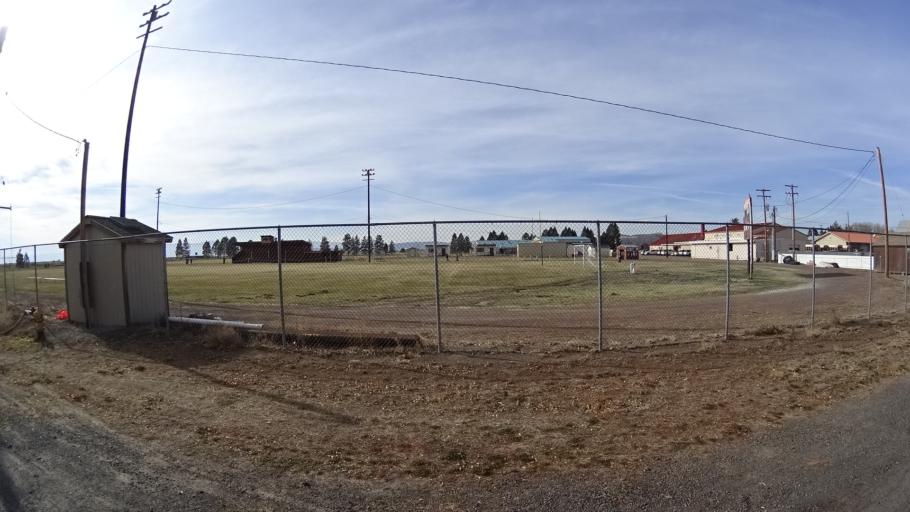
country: US
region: Oregon
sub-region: Klamath County
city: Klamath Falls
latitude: 41.9630
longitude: -121.9227
